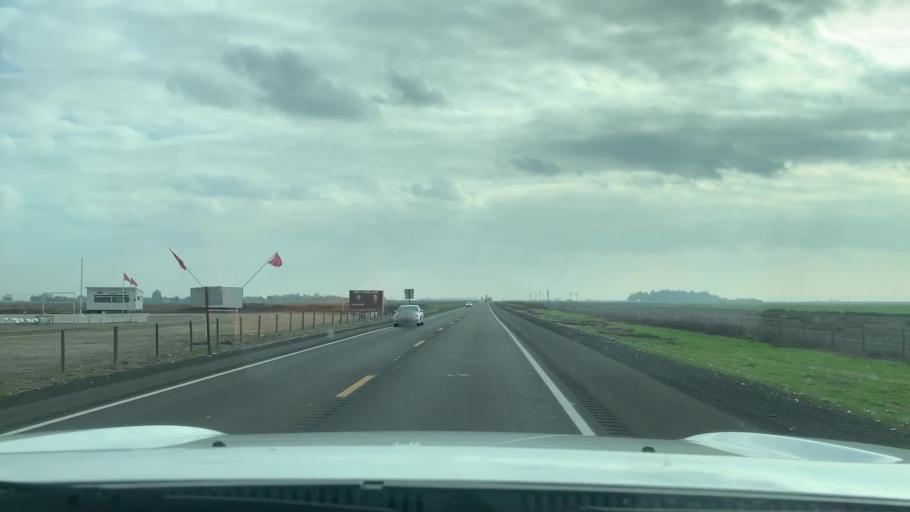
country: US
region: California
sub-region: Kings County
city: Lemoore
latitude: 36.2668
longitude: -119.8076
